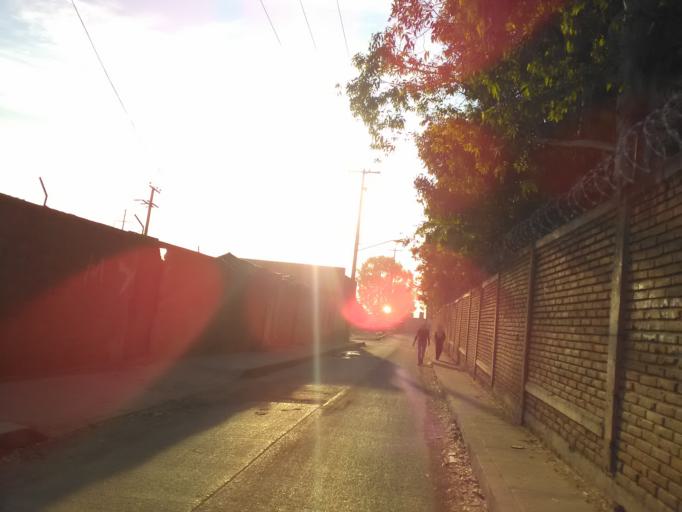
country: MX
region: Durango
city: Victoria de Durango
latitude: 24.0463
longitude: -104.6665
